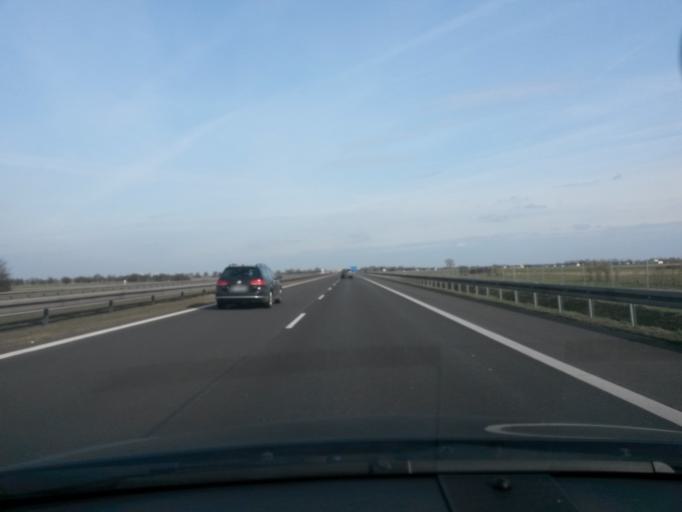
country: PL
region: Greater Poland Voivodeship
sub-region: Powiat slupecki
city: Ladek
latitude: 52.2118
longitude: 17.9892
